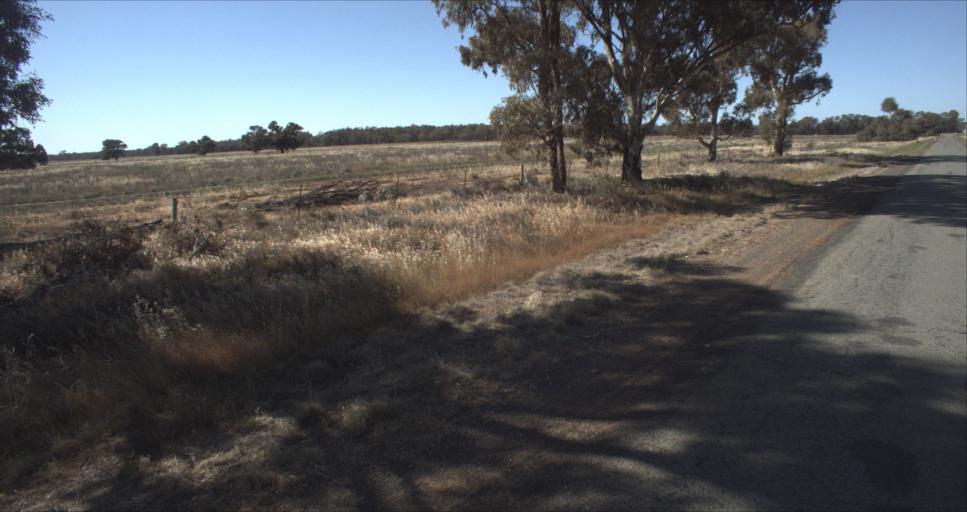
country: AU
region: New South Wales
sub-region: Leeton
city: Leeton
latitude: -34.5981
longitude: 146.2583
